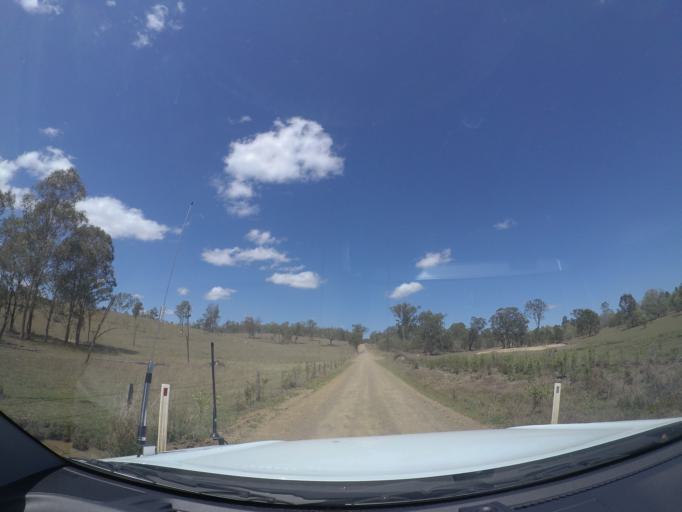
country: AU
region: Queensland
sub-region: Logan
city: Cedar Vale
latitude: -27.8525
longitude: 152.8868
